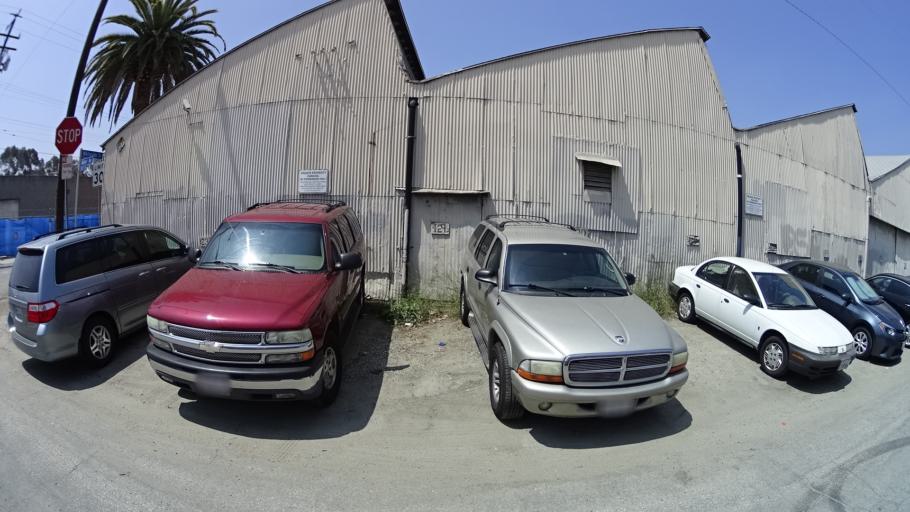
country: US
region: California
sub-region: Los Angeles County
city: Belvedere
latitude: 34.0595
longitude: -118.1791
